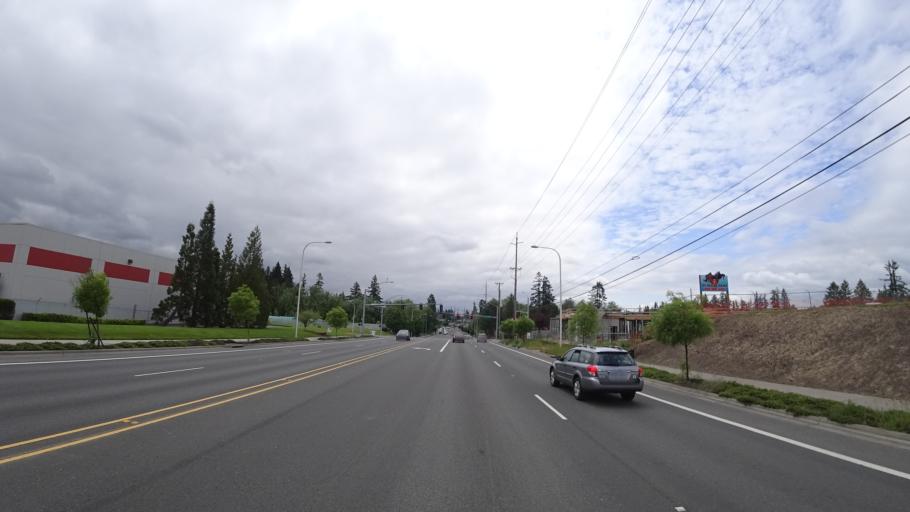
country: US
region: Oregon
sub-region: Washington County
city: Rockcreek
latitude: 45.5312
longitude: -122.8997
